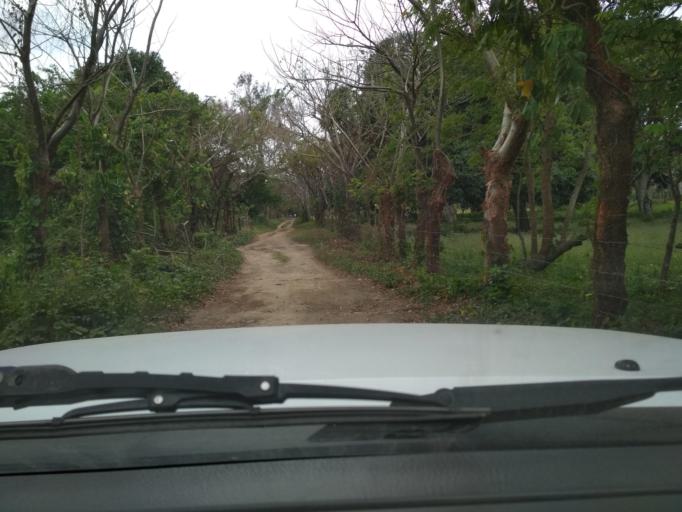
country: MX
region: Veracruz
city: El Tejar
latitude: 19.0638
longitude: -96.1523
